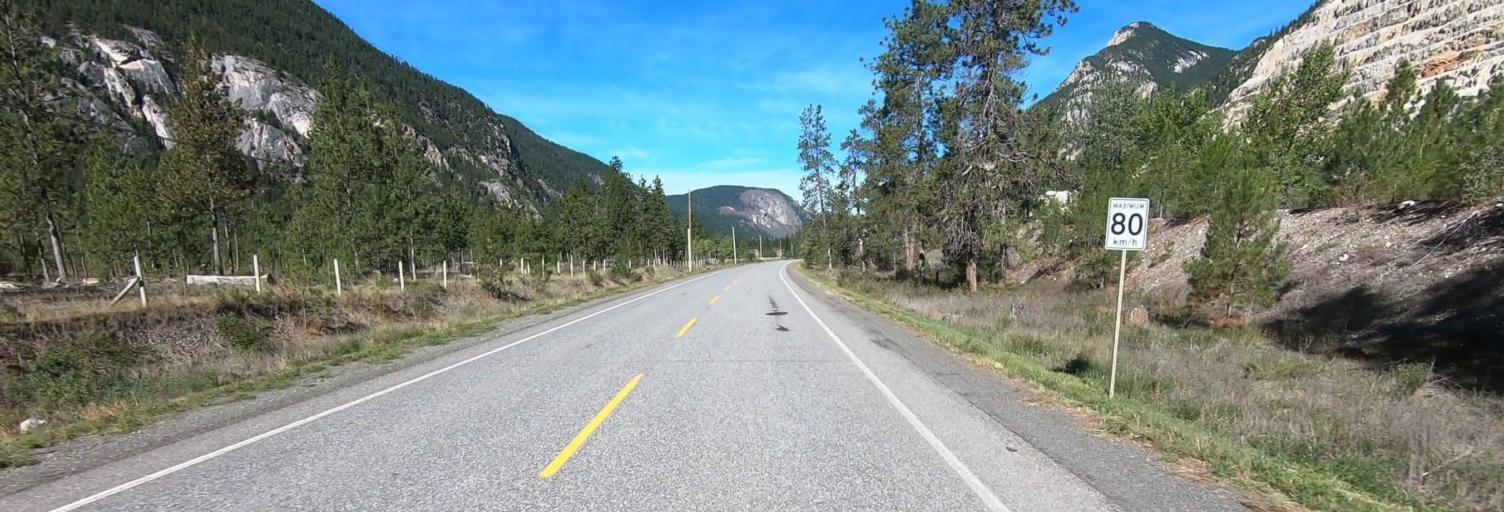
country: CA
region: British Columbia
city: Lillooet
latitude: 50.8149
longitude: -121.6522
